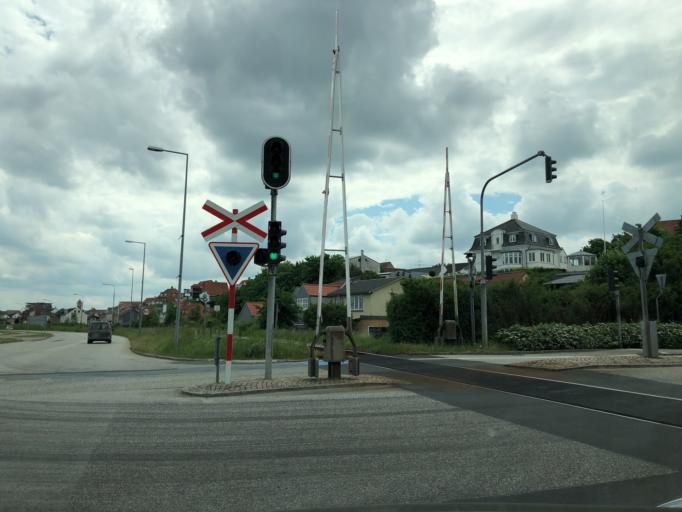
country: DK
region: Central Jutland
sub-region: Struer Kommune
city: Struer
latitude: 56.4940
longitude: 8.5858
